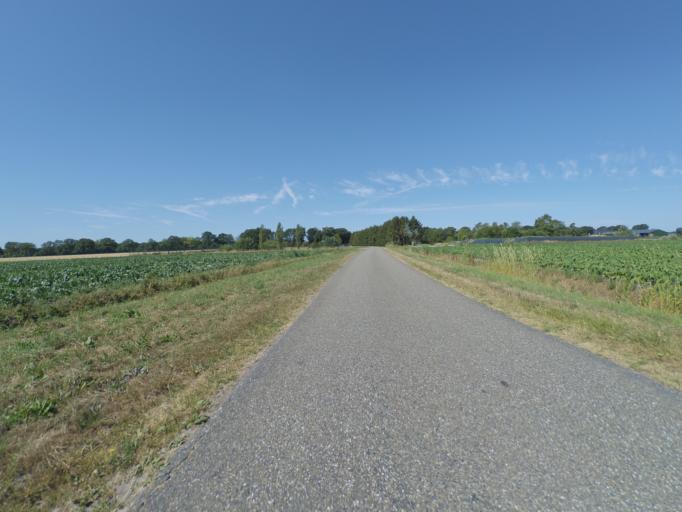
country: NL
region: Drenthe
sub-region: Gemeente Aa en Hunze
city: Anloo
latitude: 52.9500
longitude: 6.6716
